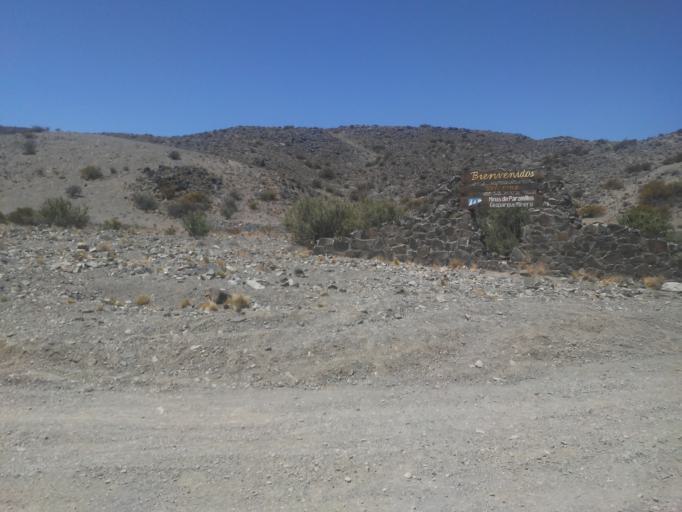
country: AR
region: Mendoza
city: Las Heras
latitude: -32.4791
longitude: -69.1598
